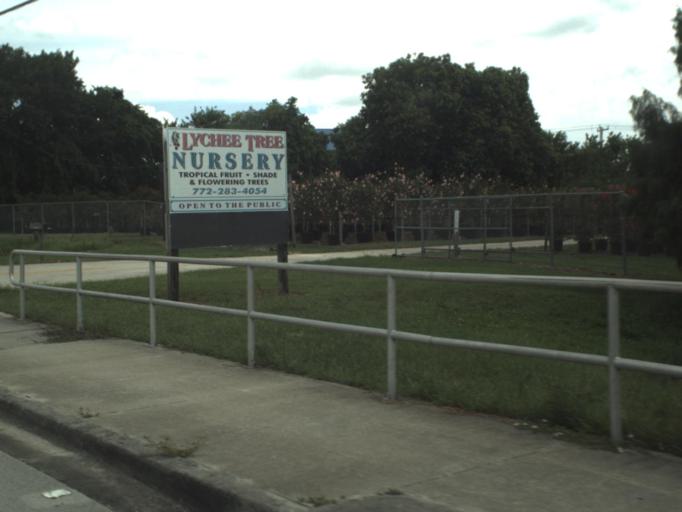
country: US
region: Florida
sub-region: Martin County
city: Palm City
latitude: 27.1675
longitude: -80.2506
